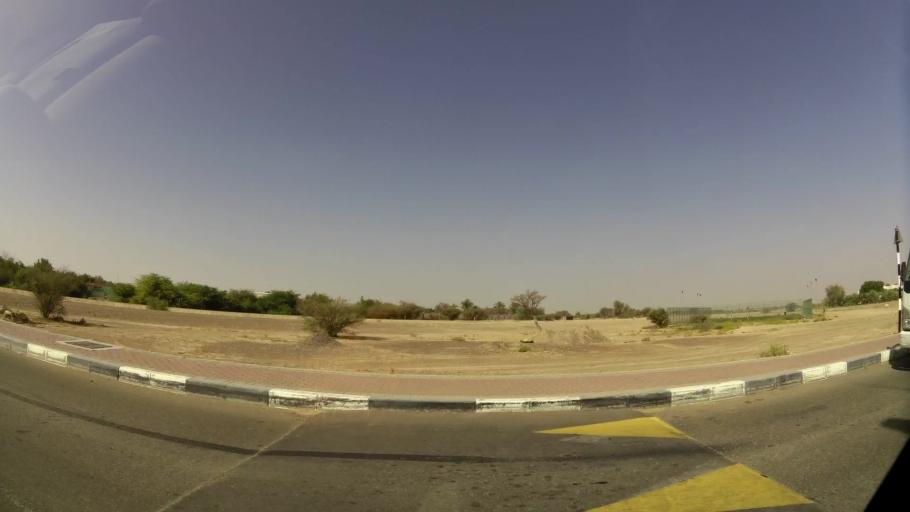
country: OM
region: Al Buraimi
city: Al Buraymi
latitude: 24.3258
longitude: 55.7948
